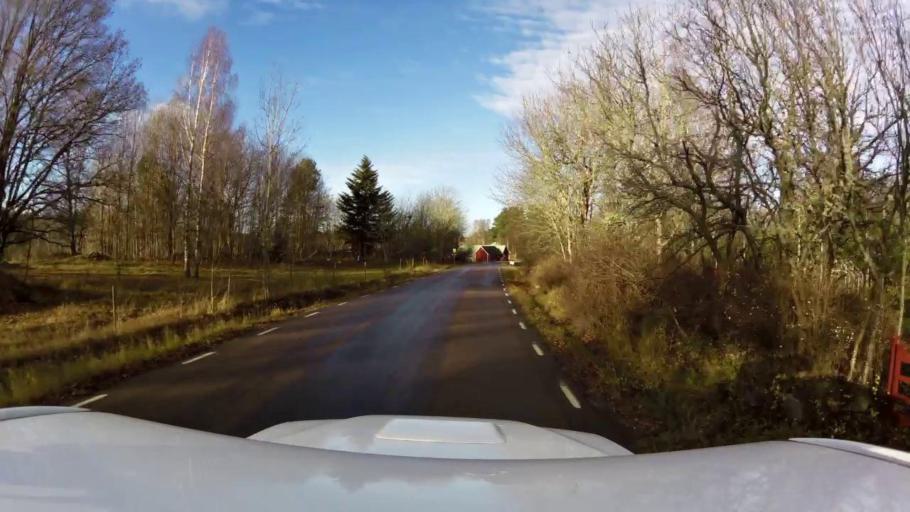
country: SE
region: OEstergoetland
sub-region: Linkopings Kommun
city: Sturefors
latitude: 58.3218
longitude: 15.6497
